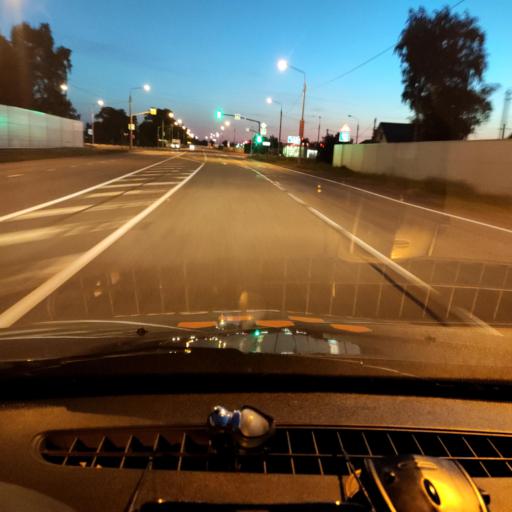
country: RU
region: Belgorod
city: Skorodnoye
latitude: 51.1865
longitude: 37.3750
